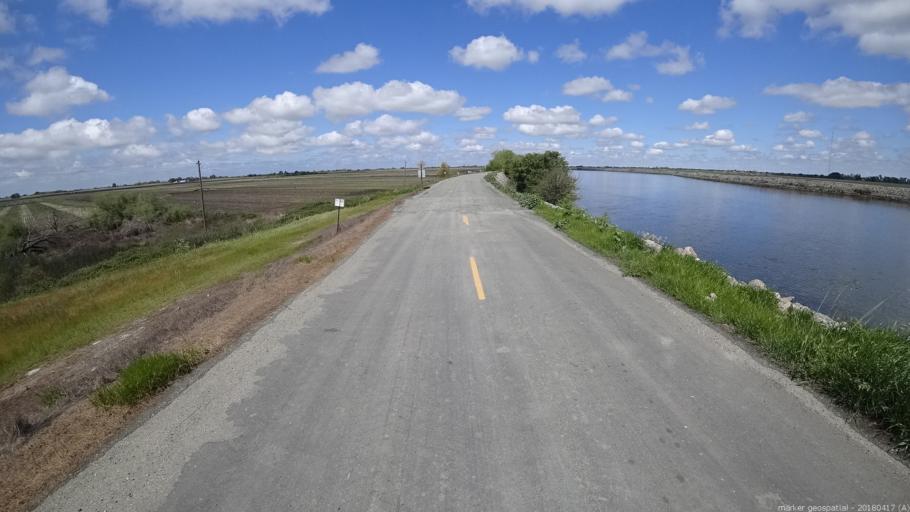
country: US
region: California
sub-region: Sacramento County
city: Walnut Grove
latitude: 38.1857
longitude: -121.5256
